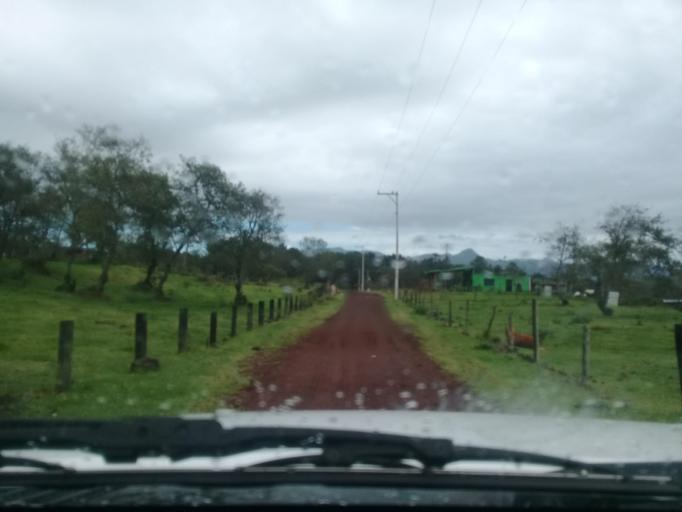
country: MX
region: Veracruz
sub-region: Acajete
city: La Joya
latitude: 19.6226
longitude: -97.0006
